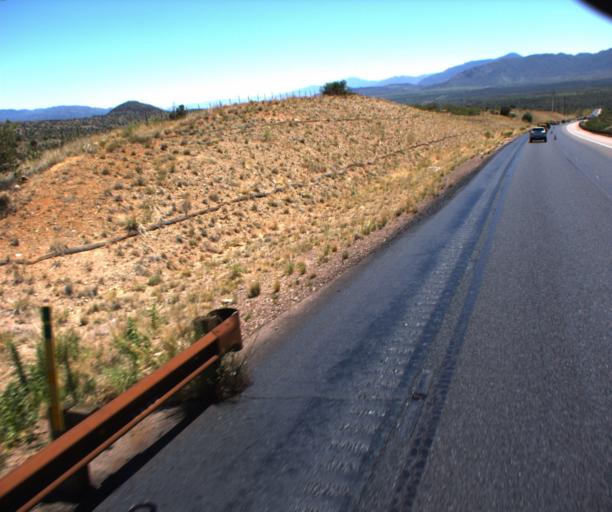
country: US
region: Arizona
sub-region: Gila County
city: Payson
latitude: 34.1406
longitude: -111.3514
